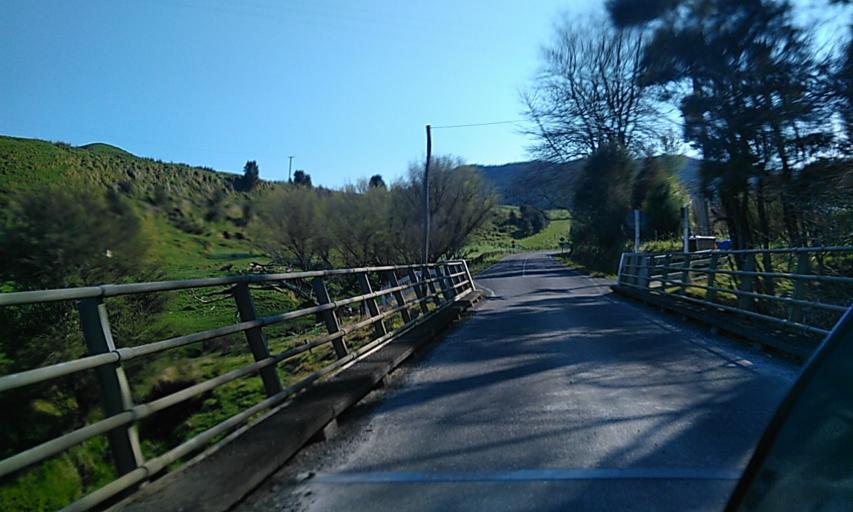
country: NZ
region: Gisborne
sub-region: Gisborne District
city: Gisborne
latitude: -38.5565
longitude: 178.0338
